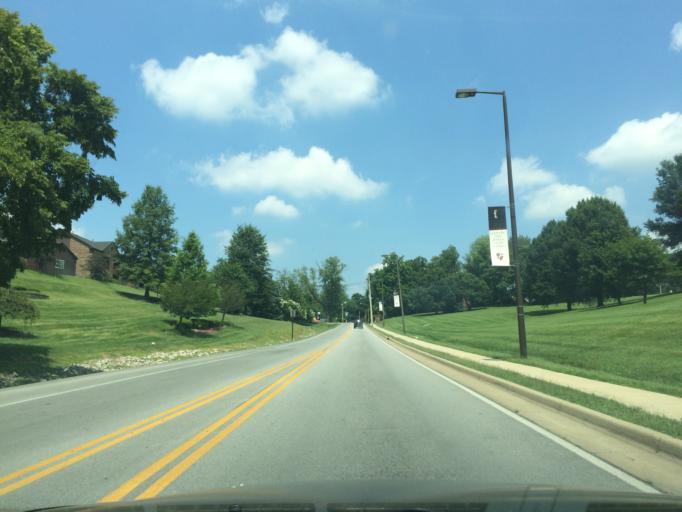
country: US
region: Kentucky
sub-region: Jefferson County
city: Audubon Park
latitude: 38.2181
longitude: -85.7086
